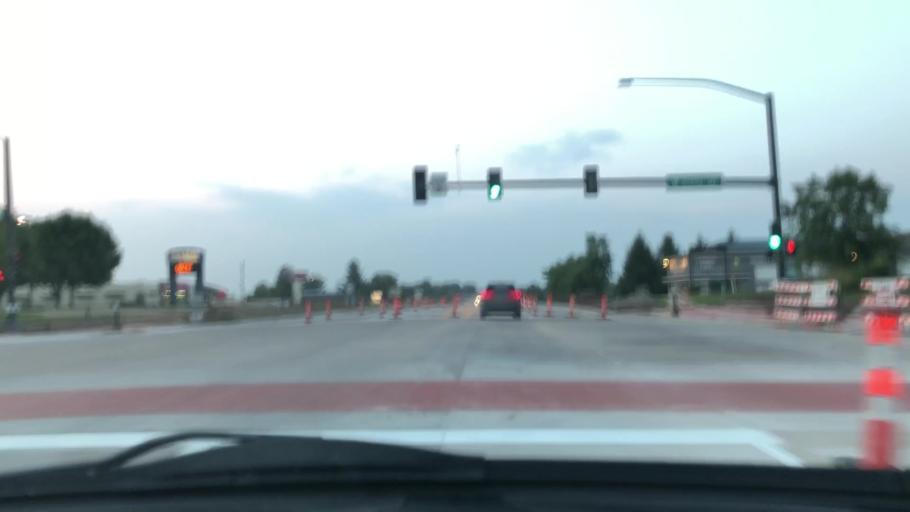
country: US
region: Iowa
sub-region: Johnson County
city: North Liberty
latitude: 41.7448
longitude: -91.6076
